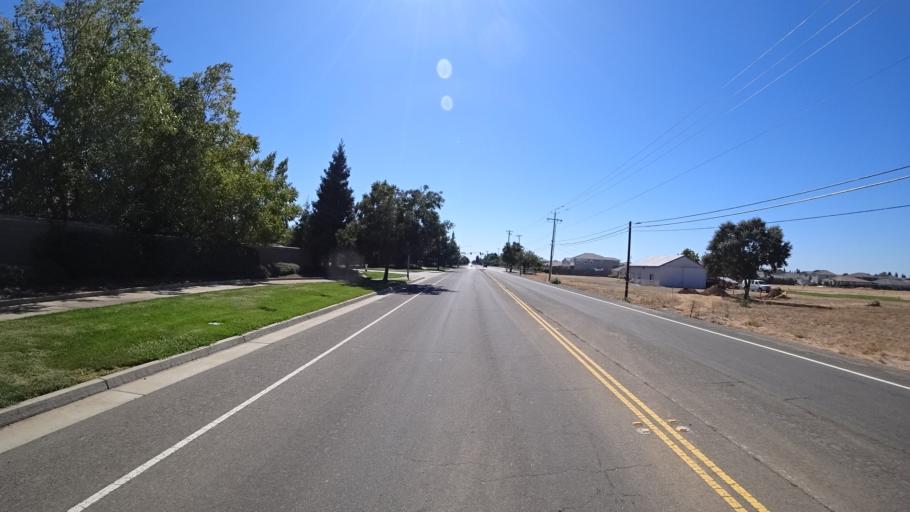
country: US
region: California
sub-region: Sacramento County
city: Elk Grove
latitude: 38.4194
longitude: -121.3346
